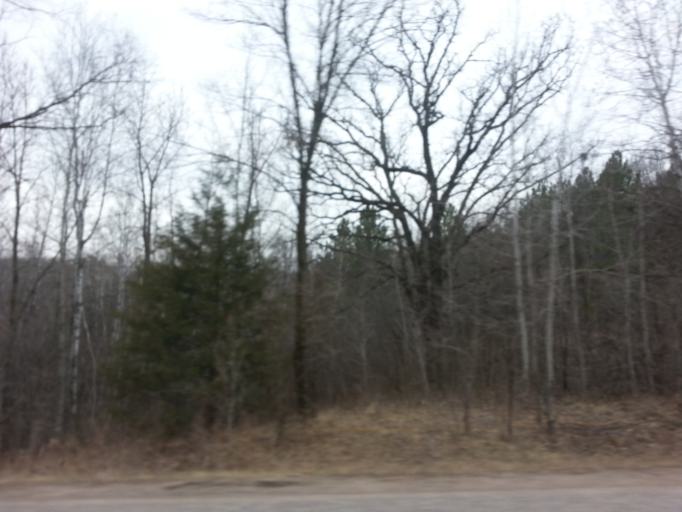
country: US
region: Wisconsin
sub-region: Saint Croix County
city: North Hudson
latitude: 45.0080
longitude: -92.7382
